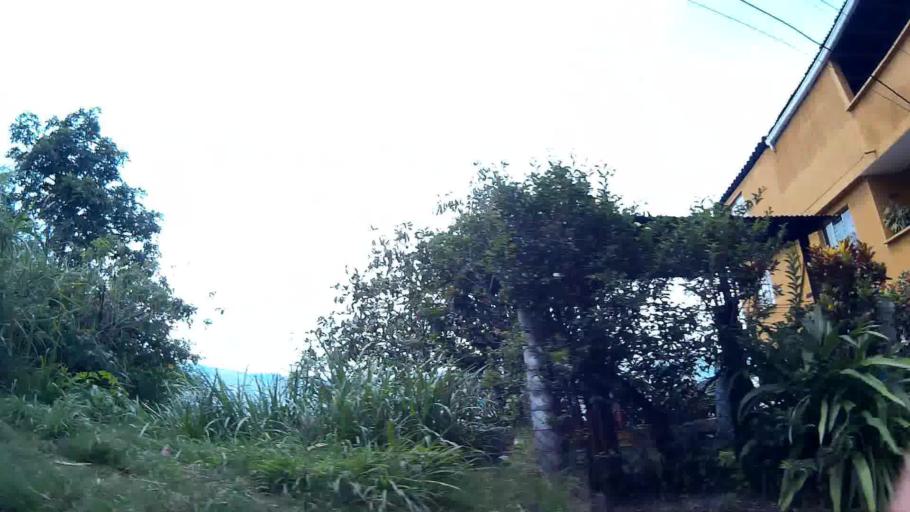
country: CO
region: Antioquia
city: Medellin
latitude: 6.2643
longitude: -75.6256
